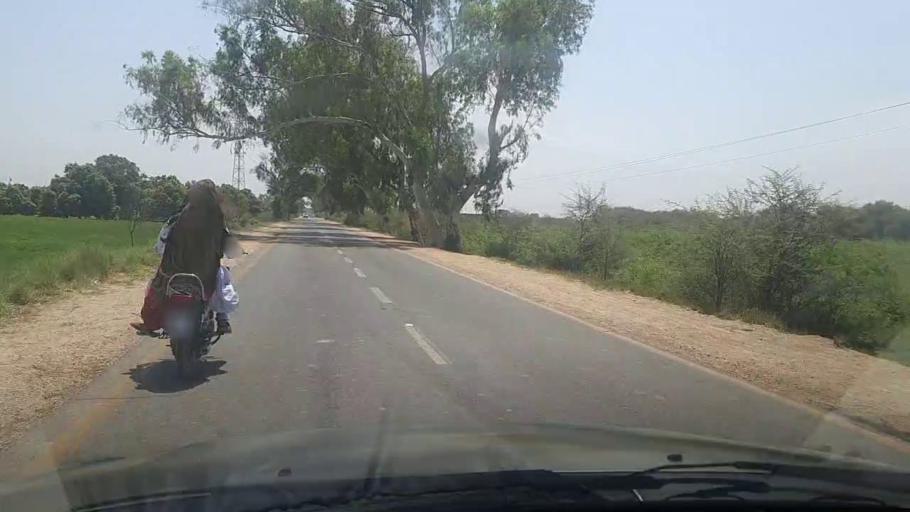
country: PK
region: Sindh
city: Tando Jam
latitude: 25.3217
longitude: 68.5538
